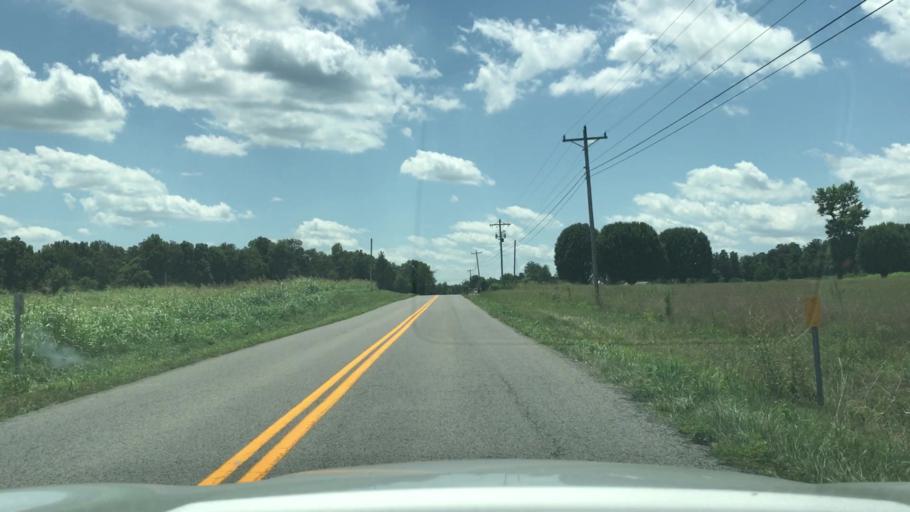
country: US
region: Kentucky
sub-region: Christian County
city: Hopkinsville
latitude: 36.9784
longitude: -87.3641
